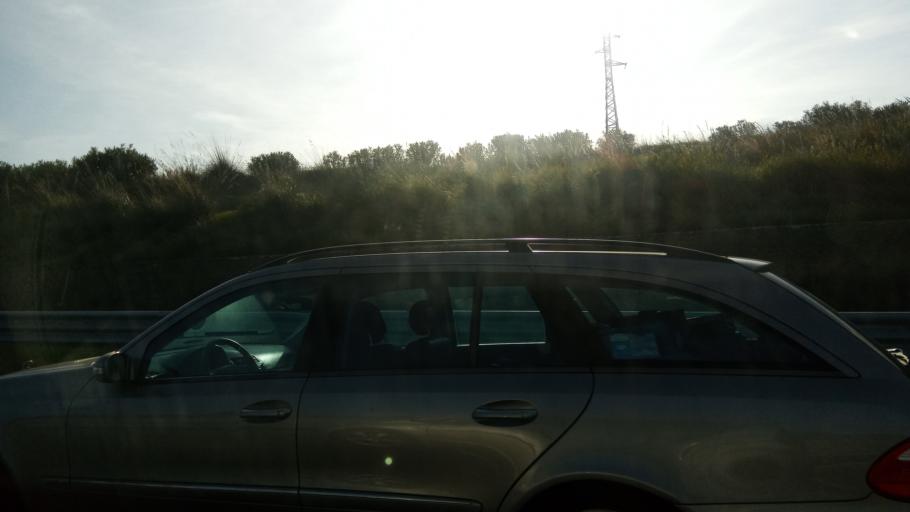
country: IT
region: Molise
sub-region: Provincia di Campobasso
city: Campomarino
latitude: 41.9500
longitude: 15.0220
